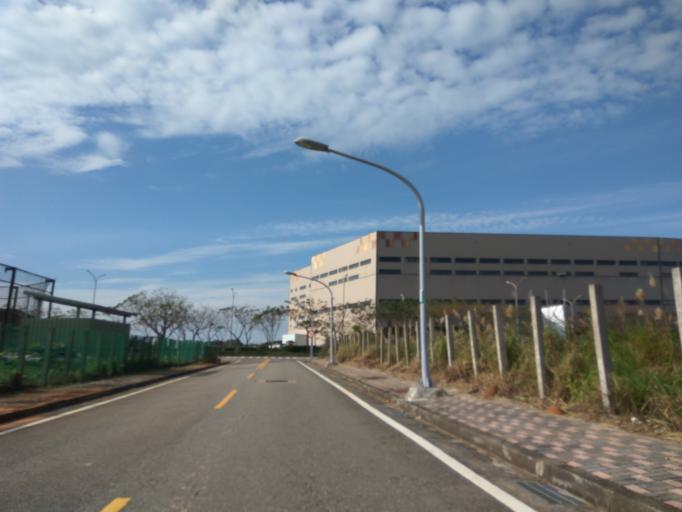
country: TW
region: Taiwan
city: Taoyuan City
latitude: 25.0539
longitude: 121.1772
